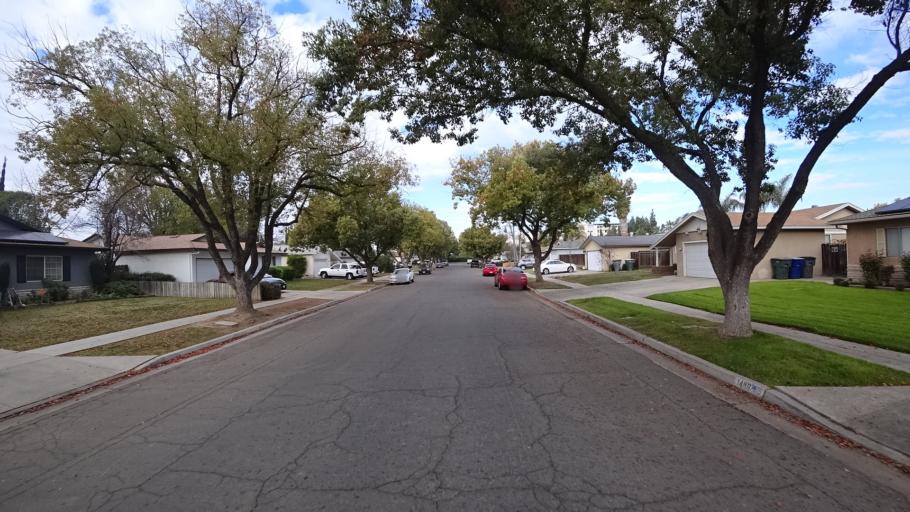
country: US
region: California
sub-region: Fresno County
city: Clovis
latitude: 36.8346
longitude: -119.7611
